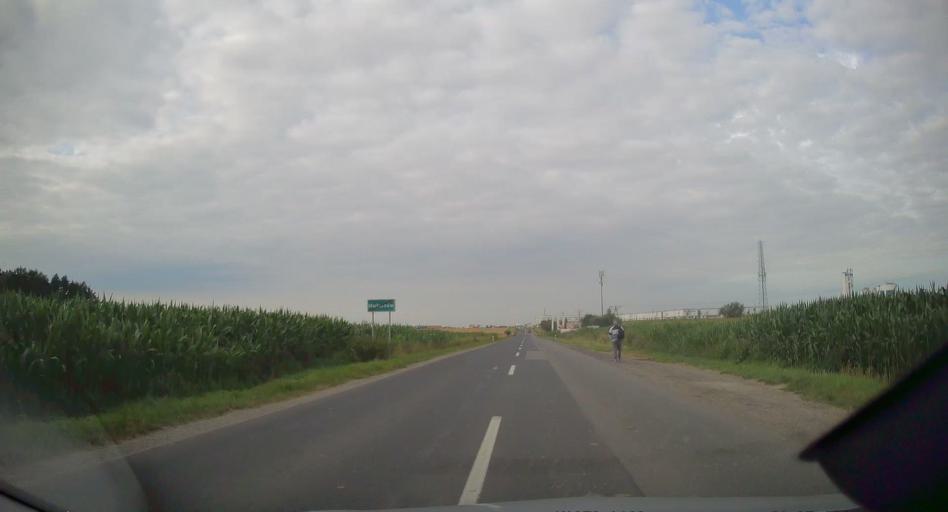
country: PL
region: Lower Silesian Voivodeship
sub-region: Powiat wroclawski
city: Tyniec Maly
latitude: 51.0142
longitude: 16.8737
